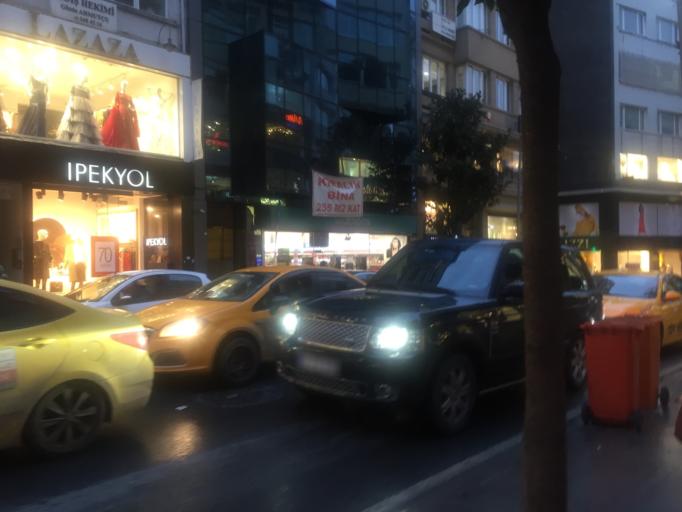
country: TR
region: Istanbul
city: Sisli
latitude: 41.0529
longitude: 28.9899
